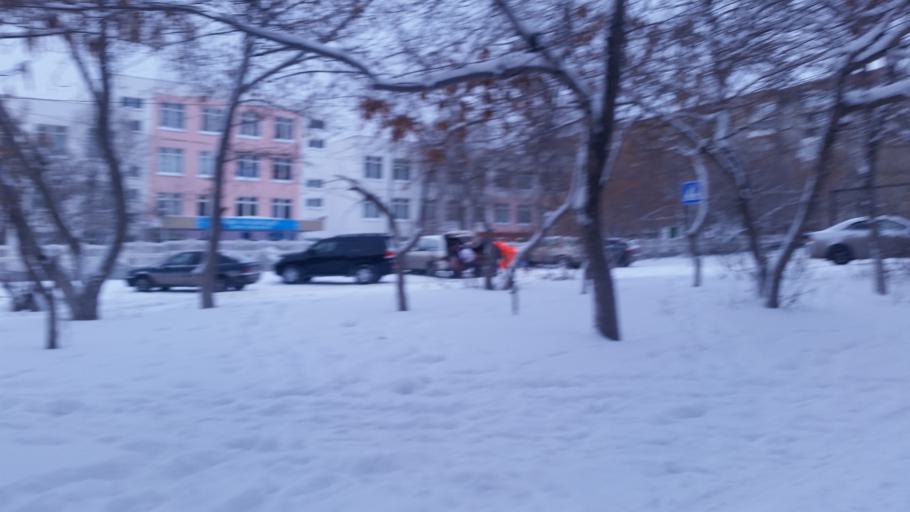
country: KZ
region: Qaraghandy
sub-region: Qaraghandy Qalasy
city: Karagandy
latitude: 49.7721
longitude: 73.1532
